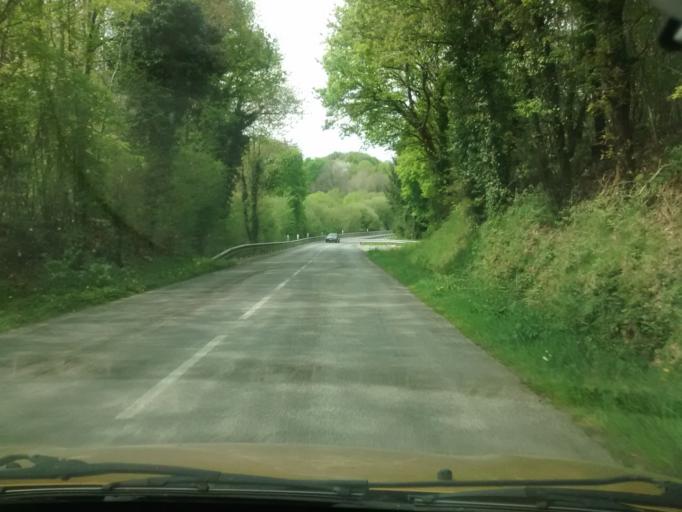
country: FR
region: Brittany
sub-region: Departement du Morbihan
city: Berric
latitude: 47.6437
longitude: -2.5062
